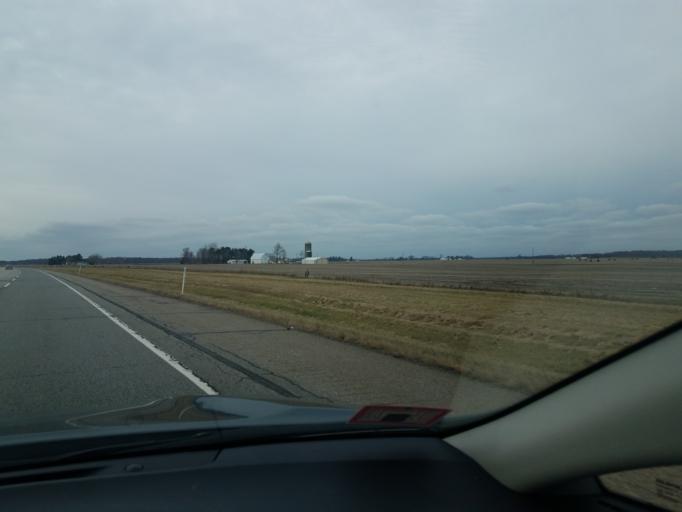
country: US
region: Michigan
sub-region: Saint Joseph County
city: Sturgis
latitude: 41.7483
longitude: -85.3382
